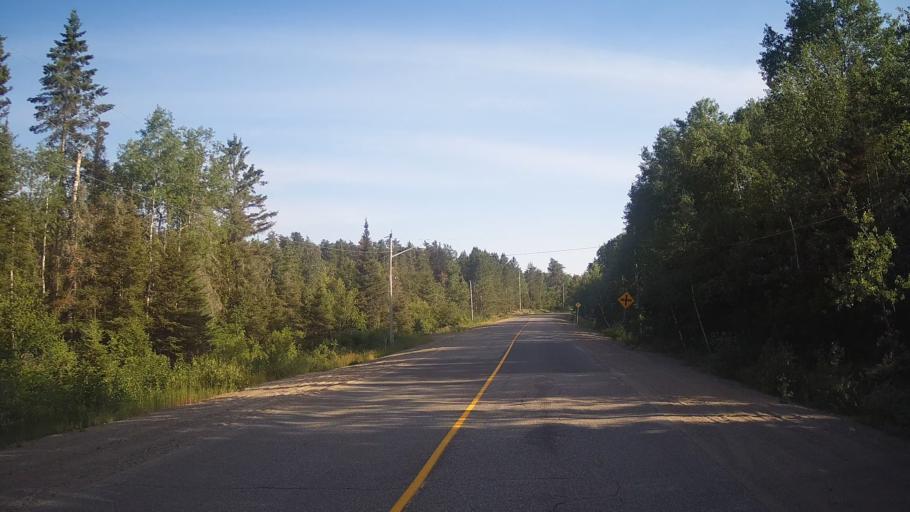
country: CA
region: Ontario
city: Rayside-Balfour
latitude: 46.5763
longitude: -81.3083
